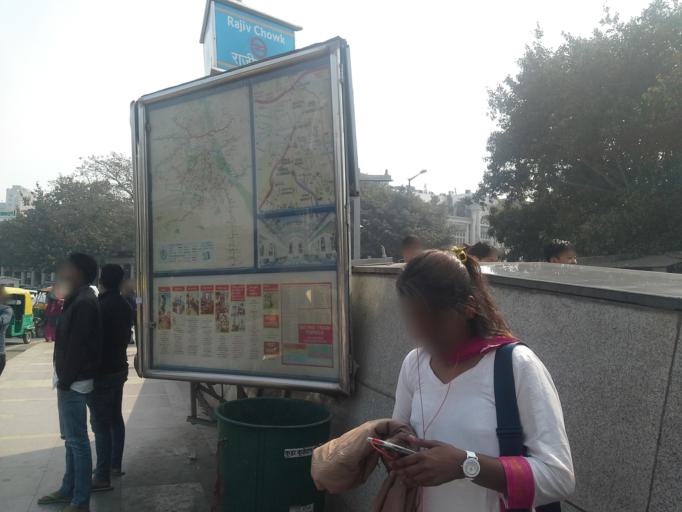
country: IN
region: NCT
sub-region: New Delhi
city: New Delhi
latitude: 28.6316
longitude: 77.2193
